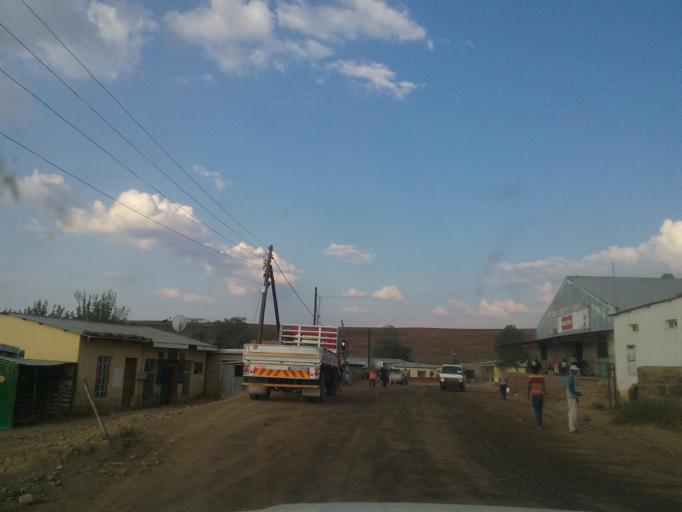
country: LS
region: Quthing
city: Quthing
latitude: -30.3950
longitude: 27.6246
